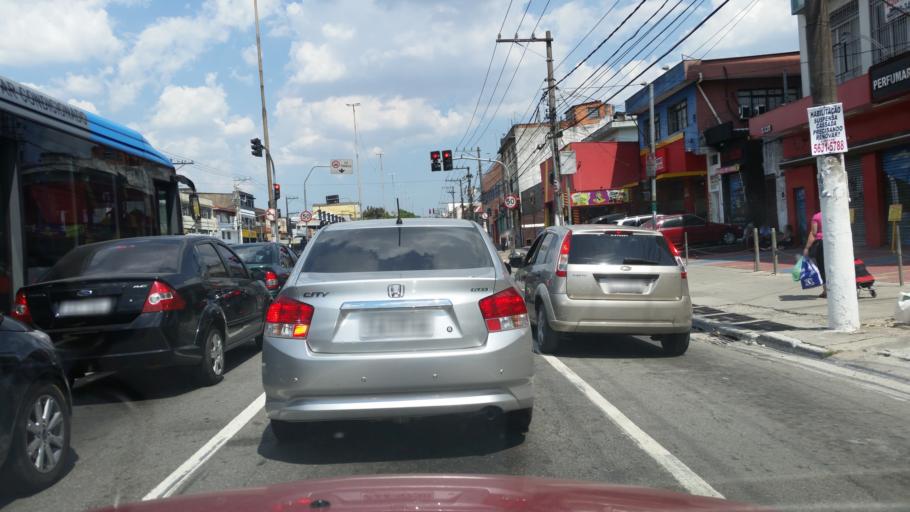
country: BR
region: Sao Paulo
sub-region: Diadema
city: Diadema
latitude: -23.6675
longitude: -46.6535
